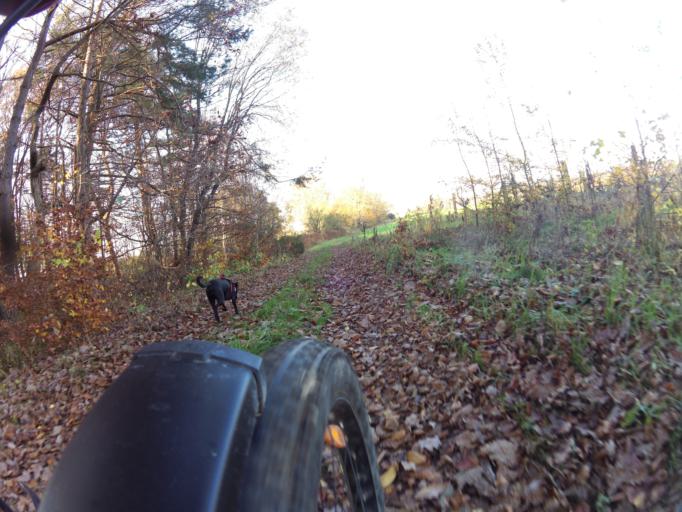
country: PL
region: Pomeranian Voivodeship
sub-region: Powiat pucki
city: Krokowa
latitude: 54.7303
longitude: 18.1983
